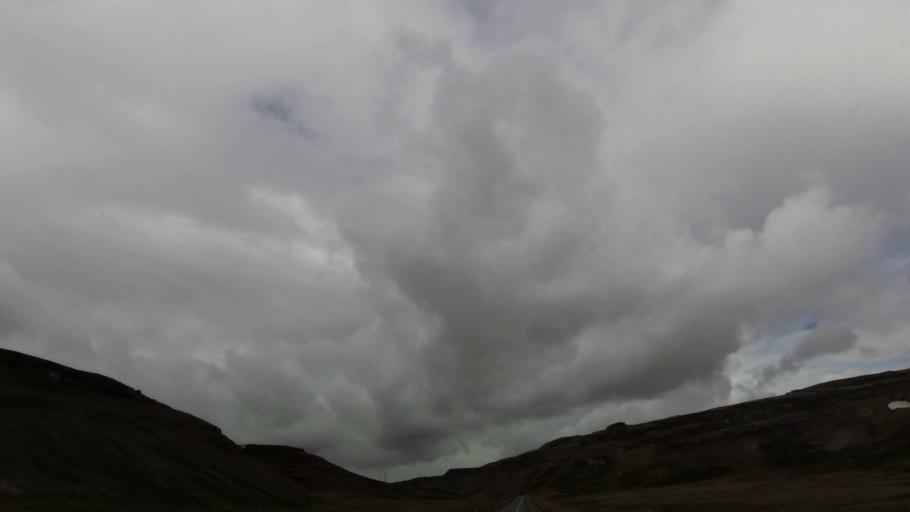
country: IS
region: West
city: Borgarnes
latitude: 65.3014
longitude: -21.7430
